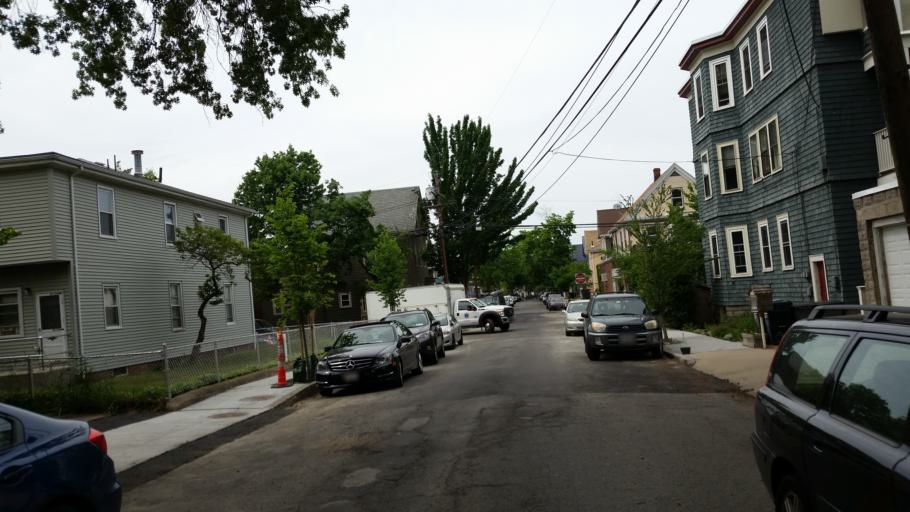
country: US
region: Massachusetts
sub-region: Middlesex County
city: Arlington
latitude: 42.3954
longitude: -71.1322
